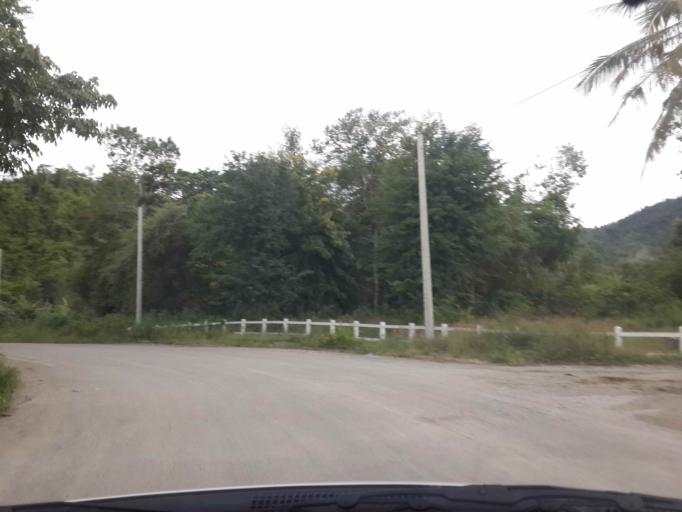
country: TH
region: Kanchanaburi
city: Dan Makham Tia
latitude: 13.7487
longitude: 99.1952
